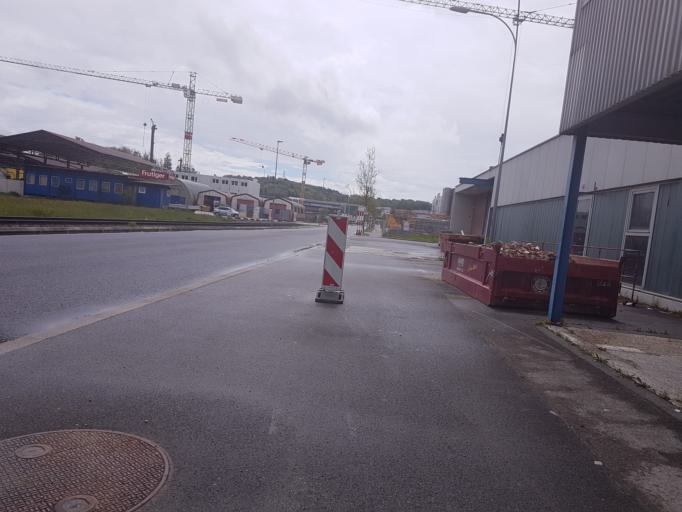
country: CH
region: Vaud
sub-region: Ouest Lausannois District
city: Bussigny
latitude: 46.5688
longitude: 6.5266
